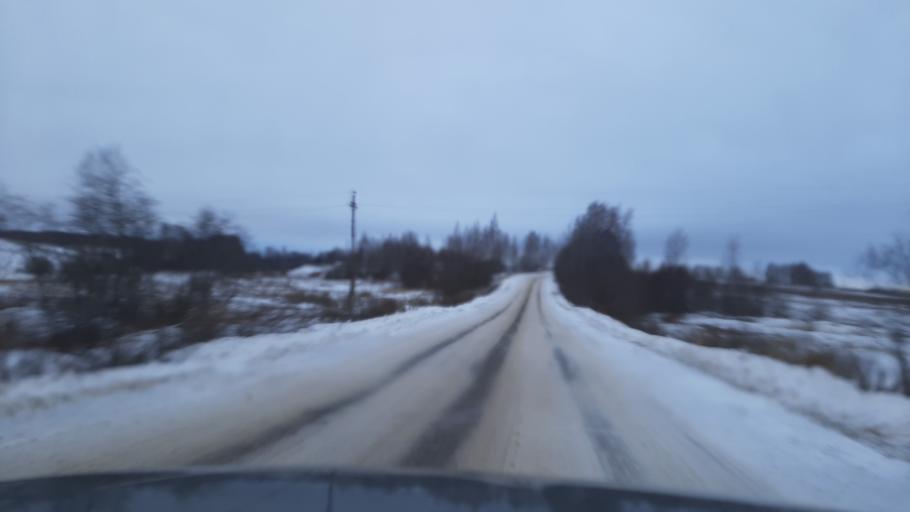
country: RU
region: Kostroma
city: Volgorechensk
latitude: 57.4373
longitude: 41.0838
